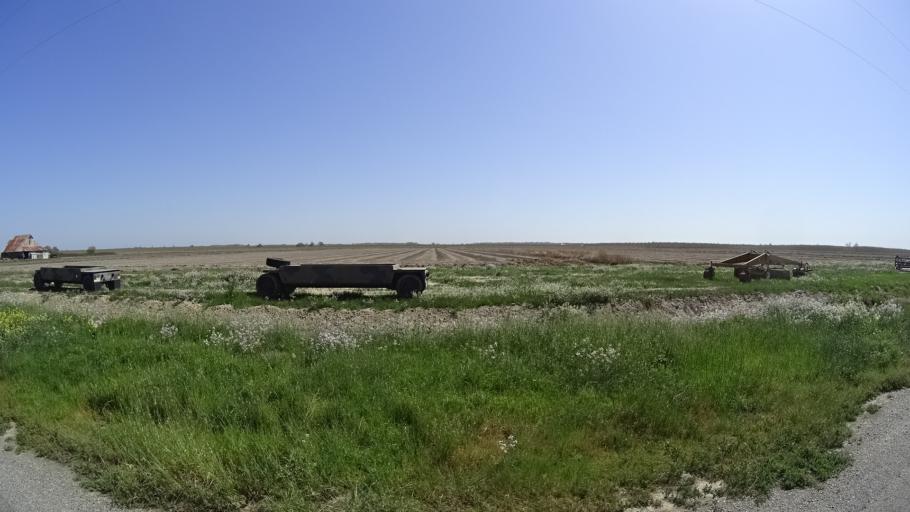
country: US
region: California
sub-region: Glenn County
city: Willows
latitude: 39.5099
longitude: -122.0373
